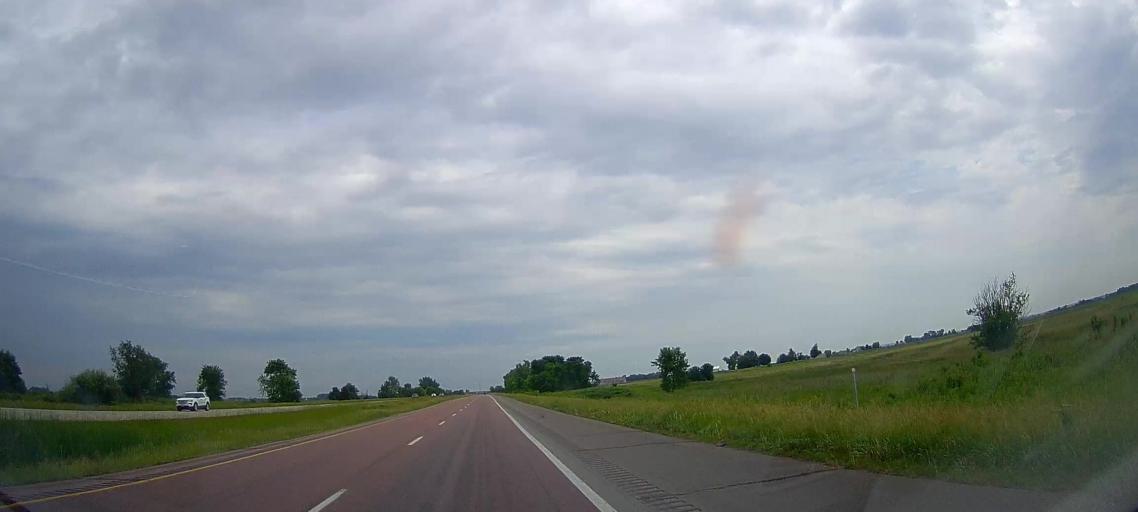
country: US
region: Iowa
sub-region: Woodbury County
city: Sergeant Bluff
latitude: 42.2691
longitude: -96.2664
